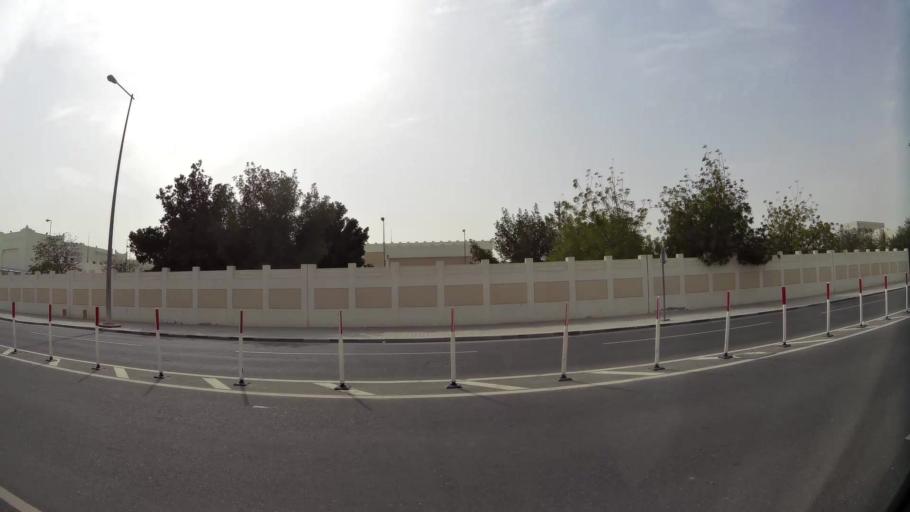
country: QA
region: Baladiyat ad Dawhah
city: Doha
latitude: 25.3215
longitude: 51.5066
